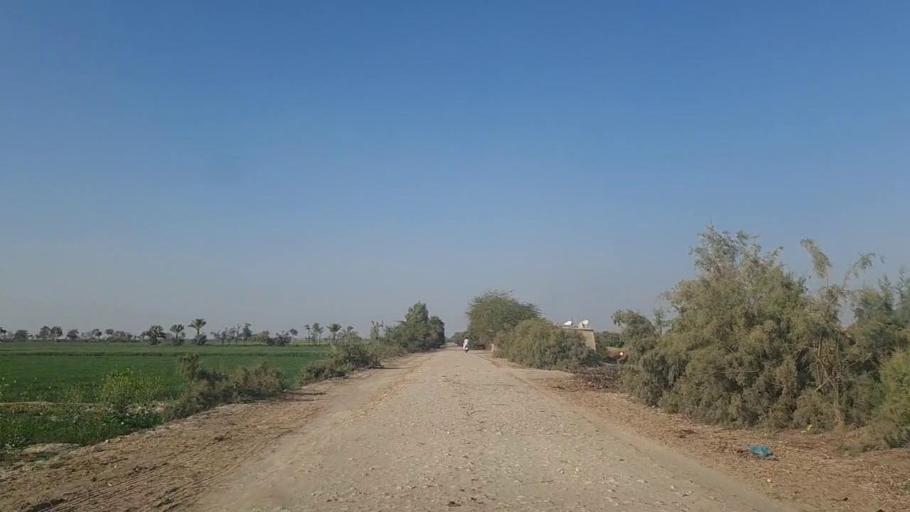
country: PK
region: Sindh
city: Jam Sahib
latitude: 26.3223
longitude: 68.7146
